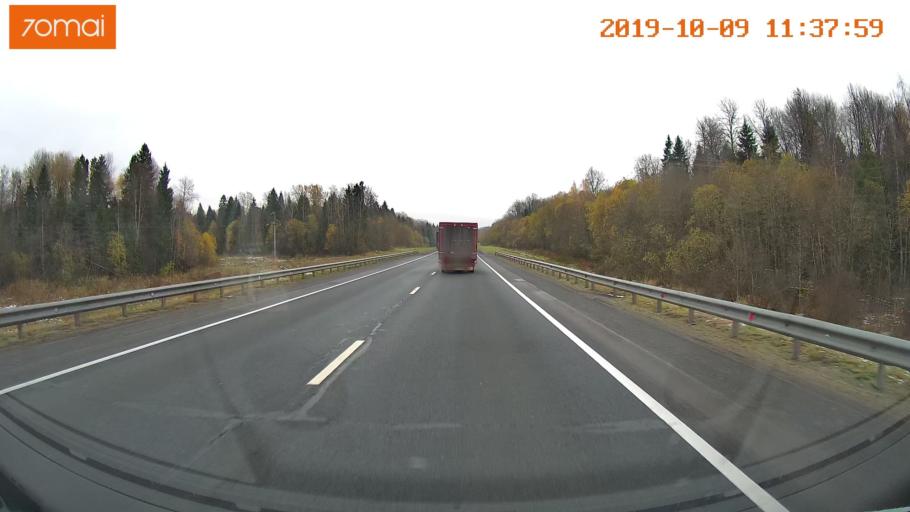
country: RU
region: Vologda
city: Gryazovets
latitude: 58.9729
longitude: 40.1518
